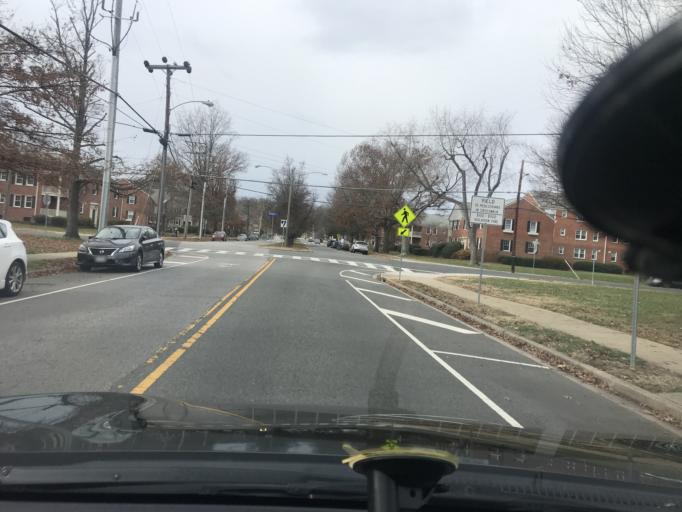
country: US
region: Virginia
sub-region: Fairfax County
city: Belle Haven
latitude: 38.7751
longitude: -77.0565
